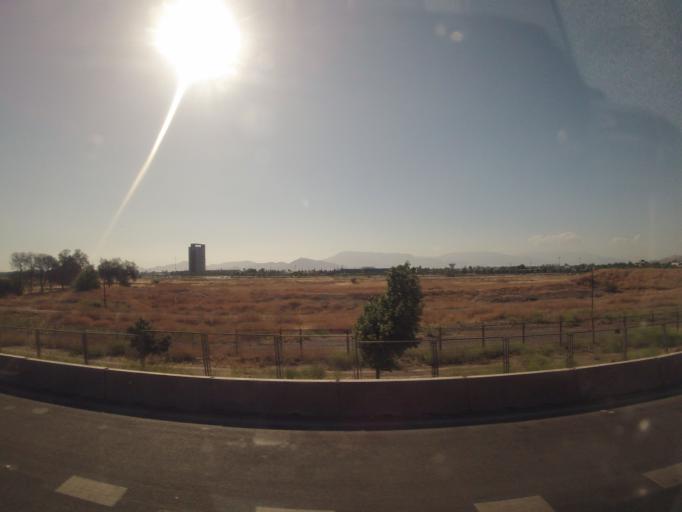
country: CL
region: Santiago Metropolitan
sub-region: Provincia de Santiago
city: Santiago
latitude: -33.4896
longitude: -70.6896
